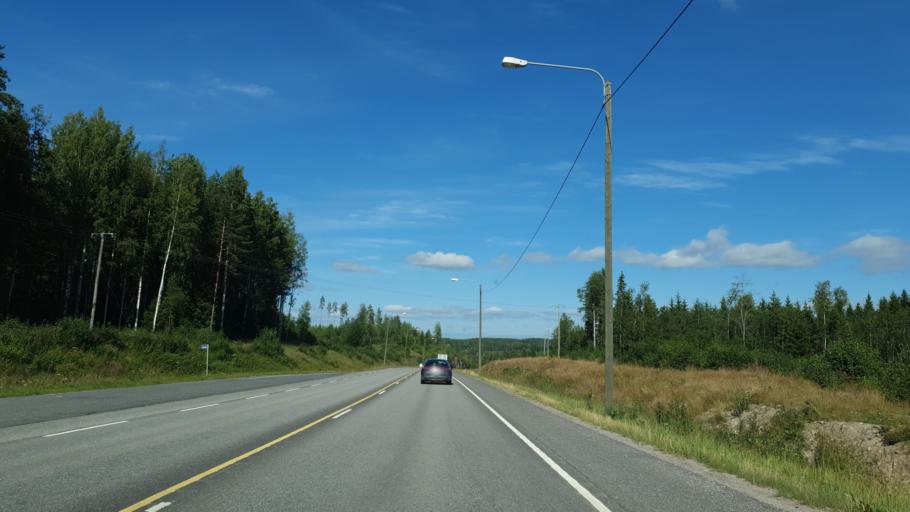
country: FI
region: Central Finland
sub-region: Jyvaeskylae
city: Toivakka
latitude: 62.2493
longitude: 26.0581
